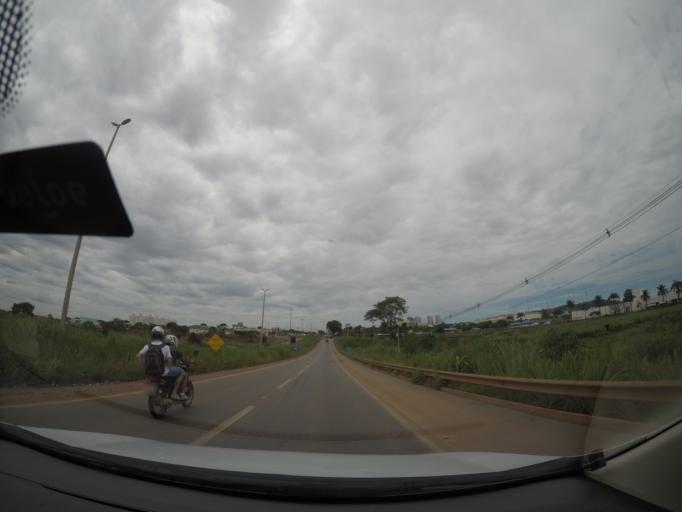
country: BR
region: Goias
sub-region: Goiania
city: Goiania
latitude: -16.6429
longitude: -49.3401
